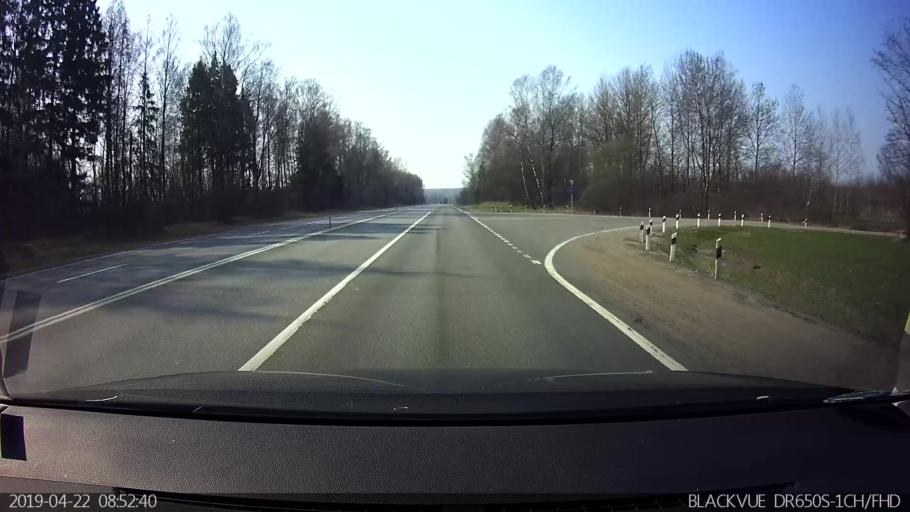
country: RU
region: Smolensk
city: Pechersk
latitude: 54.9060
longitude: 32.1229
